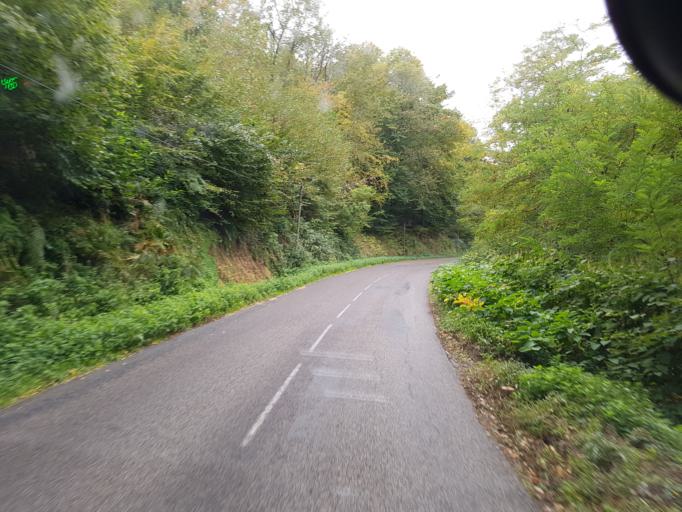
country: FR
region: Rhone-Alpes
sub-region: Departement du Rhone
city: Saint-Symphorien-sur-Coise
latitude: 45.6673
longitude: 4.4305
